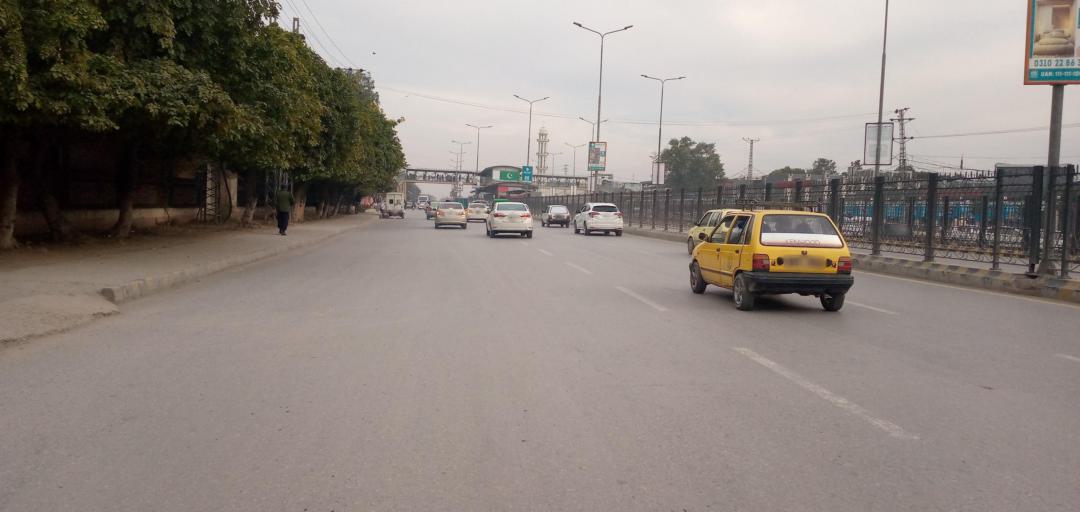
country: PK
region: Khyber Pakhtunkhwa
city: Peshawar
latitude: 33.9978
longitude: 71.4847
